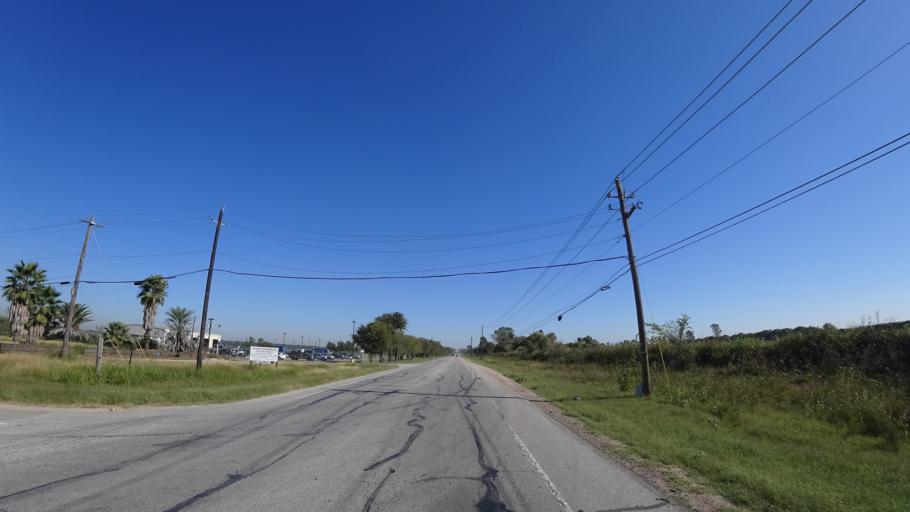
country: US
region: Texas
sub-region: Travis County
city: Hornsby Bend
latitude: 30.2414
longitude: -97.6218
